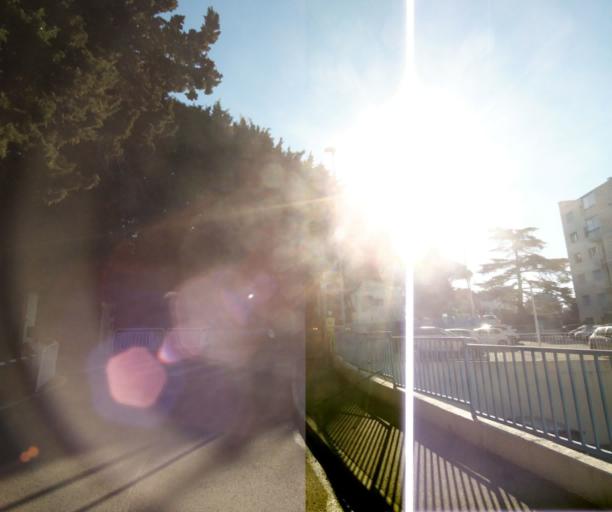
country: FR
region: Provence-Alpes-Cote d'Azur
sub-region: Departement des Alpes-Maritimes
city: Antibes
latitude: 43.5817
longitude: 7.0961
